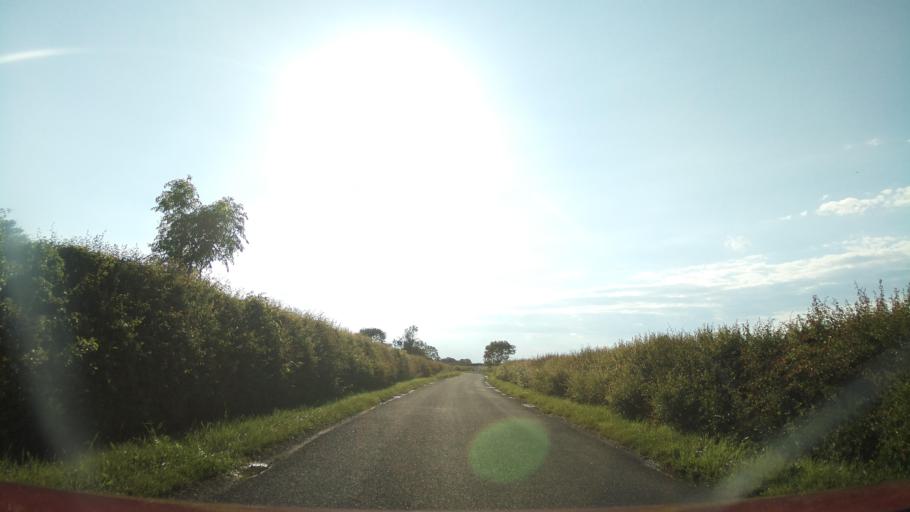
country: GB
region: England
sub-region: Lincolnshire
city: Navenby
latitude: 53.1145
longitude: -0.6106
